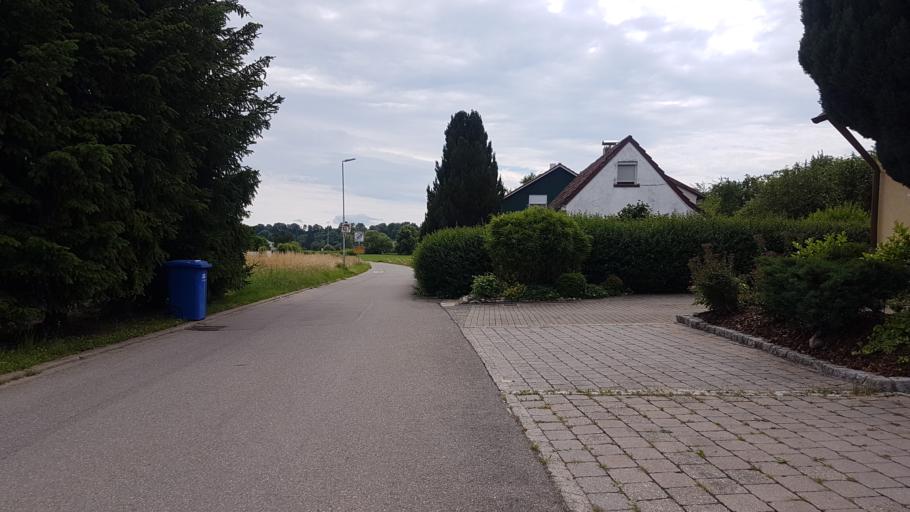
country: DE
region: Baden-Wuerttemberg
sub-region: Tuebingen Region
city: Scheer
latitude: 48.0615
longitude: 9.2988
